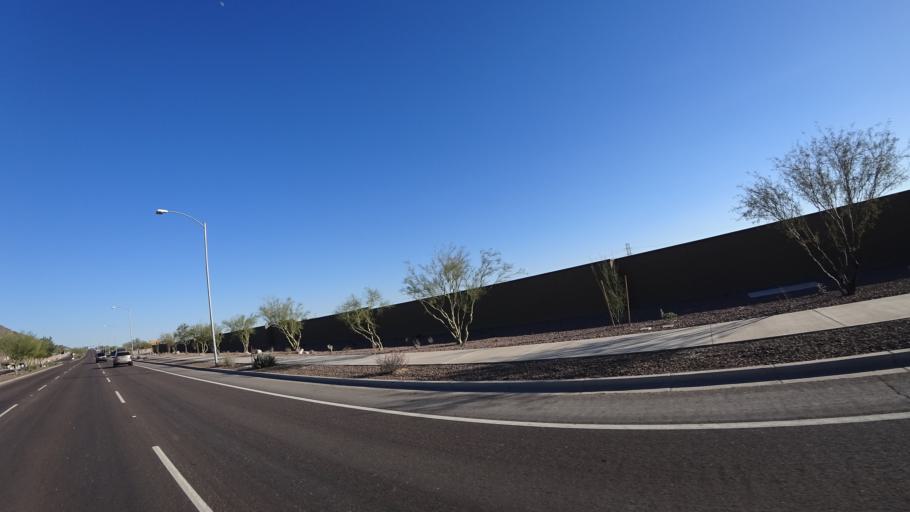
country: US
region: Arizona
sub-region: Maricopa County
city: Sun City West
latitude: 33.7106
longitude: -112.2617
